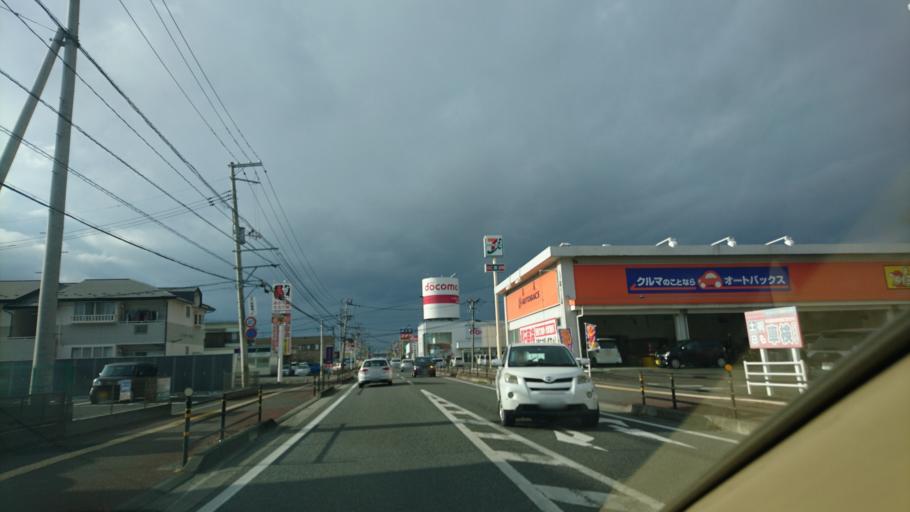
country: JP
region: Miyagi
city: Furukawa
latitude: 38.5713
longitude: 140.9771
